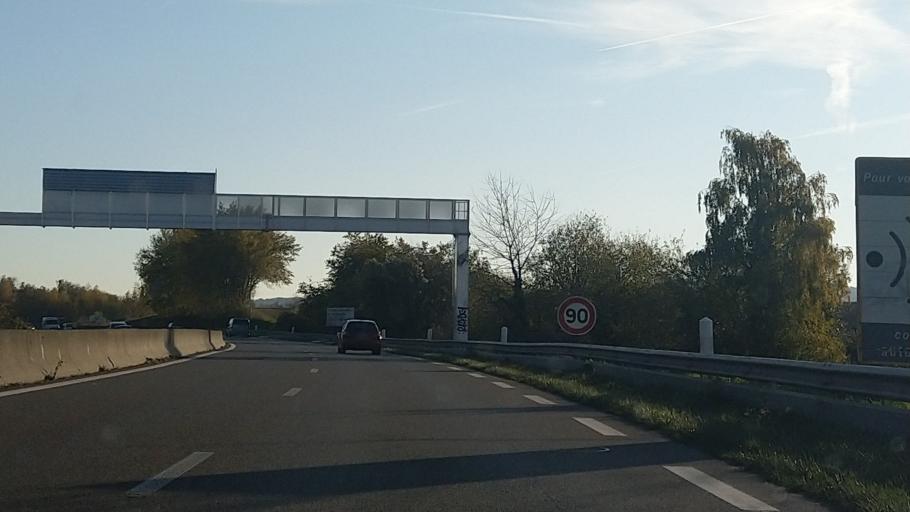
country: FR
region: Ile-de-France
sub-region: Departement du Val-d'Oise
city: Moisselles
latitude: 49.0516
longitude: 2.3301
